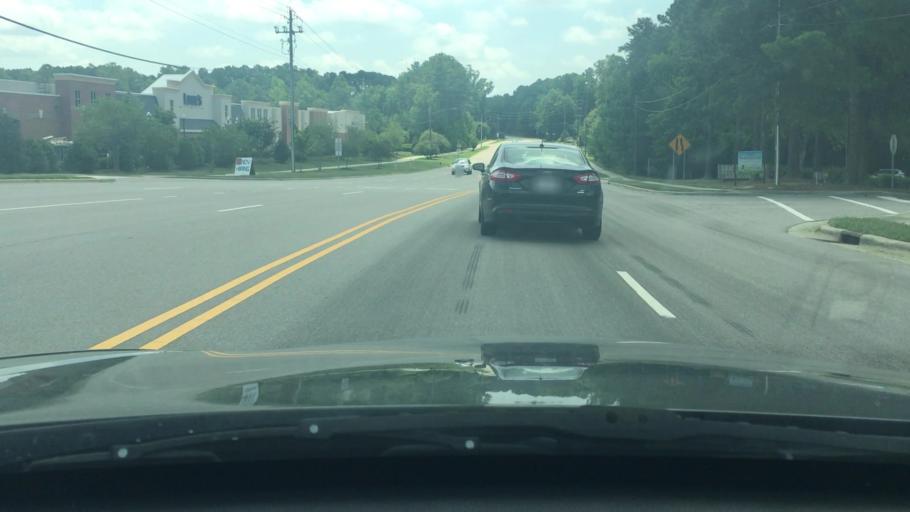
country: US
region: North Carolina
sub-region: Wake County
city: Cary
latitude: 35.7982
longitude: -78.7953
